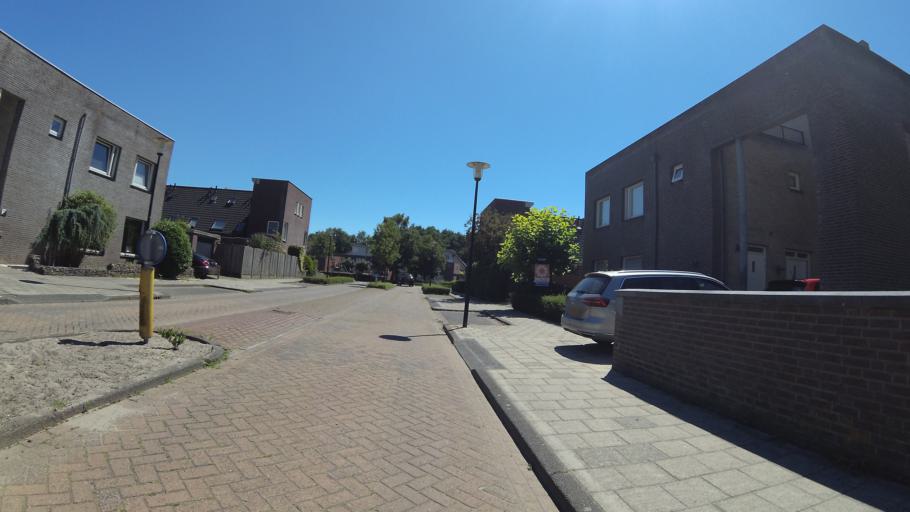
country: NL
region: North Brabant
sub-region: Gemeente Waalwijk
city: Waalwijk
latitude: 51.6727
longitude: 5.0676
